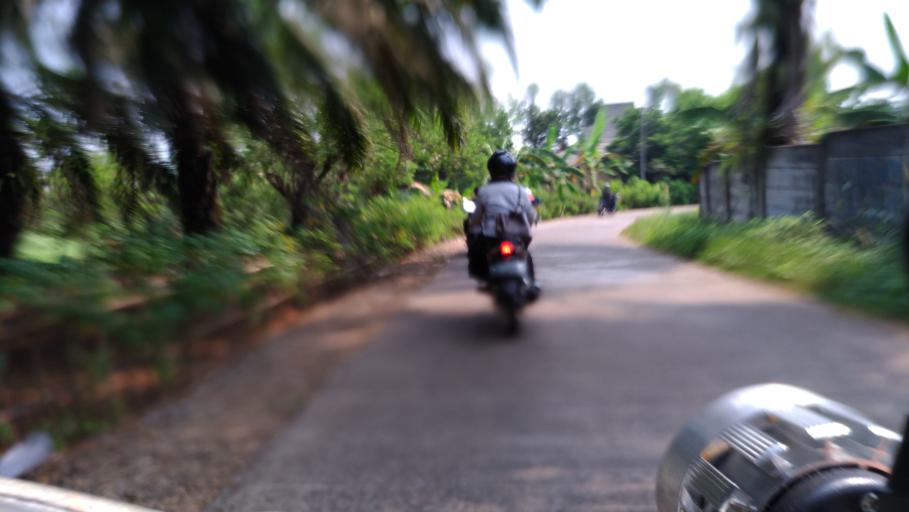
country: ID
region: West Java
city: Cileungsir
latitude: -6.3578
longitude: 106.8970
